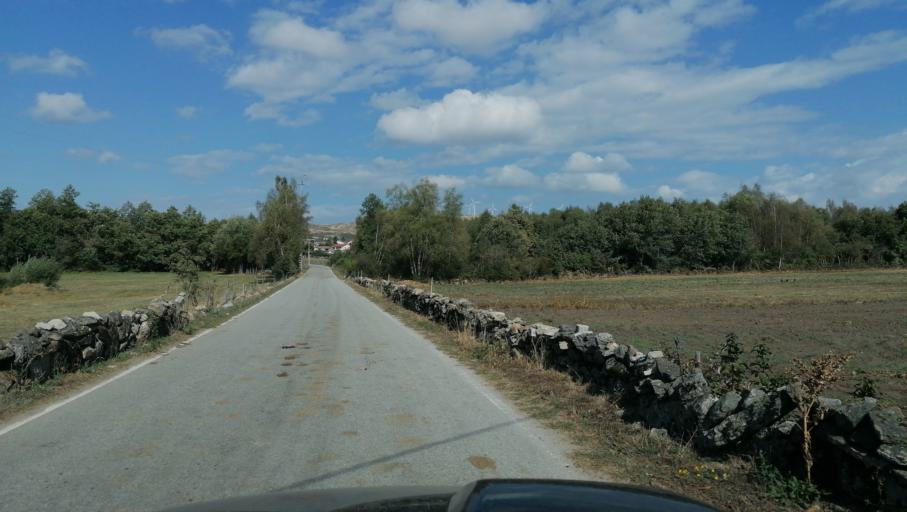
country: PT
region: Vila Real
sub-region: Vila Pouca de Aguiar
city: Vila Pouca de Aguiar
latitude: 41.5192
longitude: -7.6665
